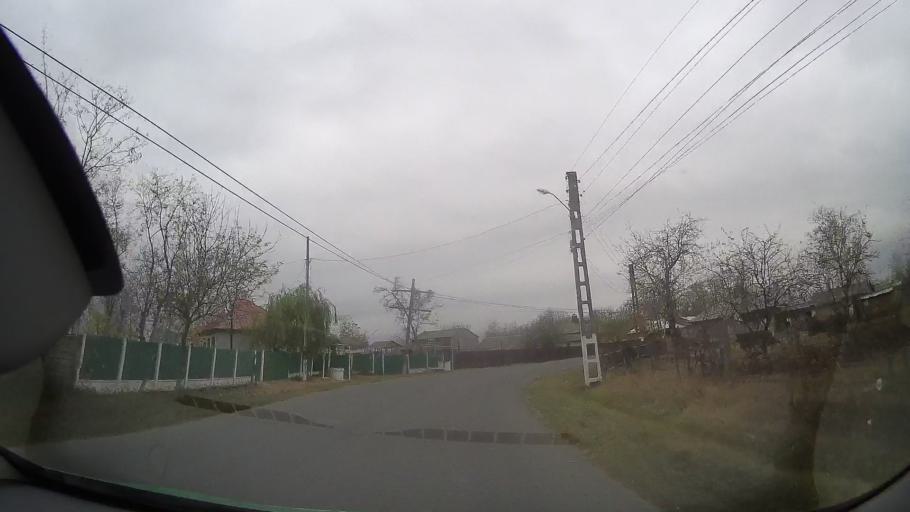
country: RO
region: Braila
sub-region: Comuna Ulmu
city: Jugureanu
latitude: 44.9424
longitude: 27.2837
